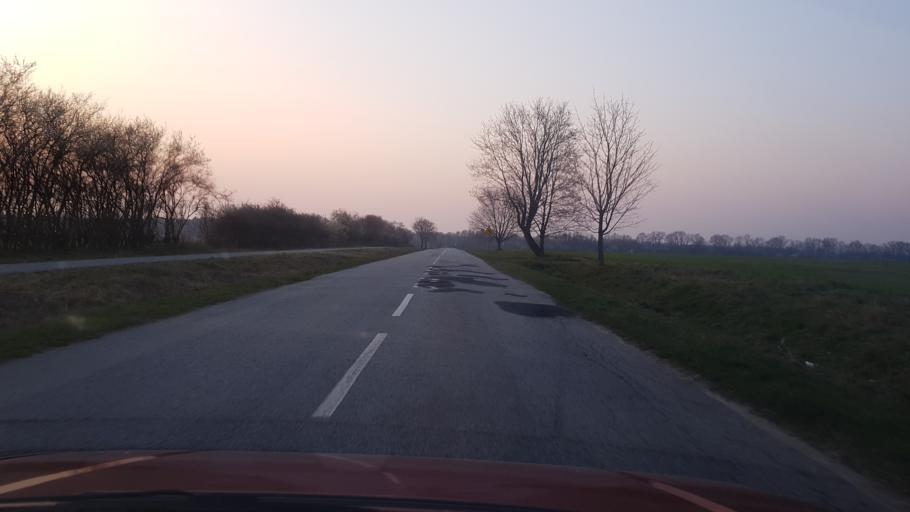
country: PL
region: West Pomeranian Voivodeship
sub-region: Powiat lobeski
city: Radowo Male
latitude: 53.6786
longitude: 15.4301
